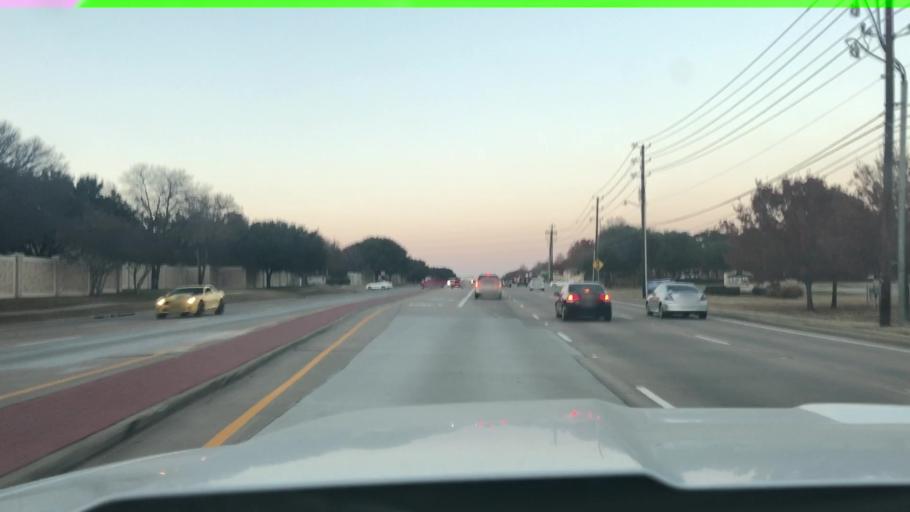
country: US
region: Texas
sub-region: Denton County
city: Flower Mound
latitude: 33.0092
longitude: -97.0708
